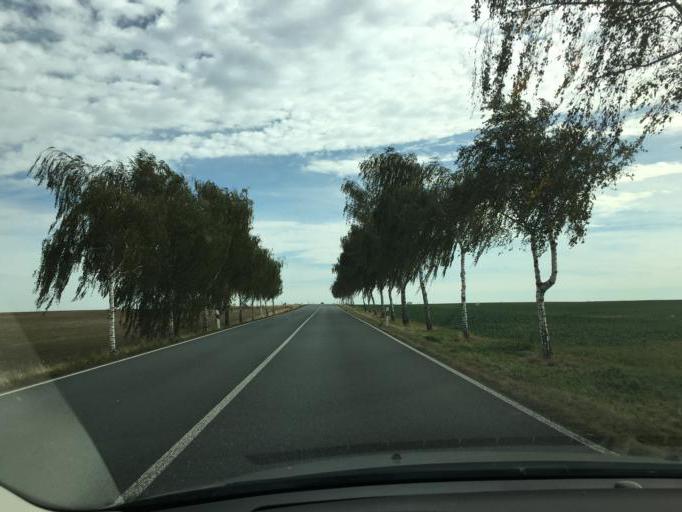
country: DE
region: Saxony
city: Stauchitz
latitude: 51.2612
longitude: 13.2653
